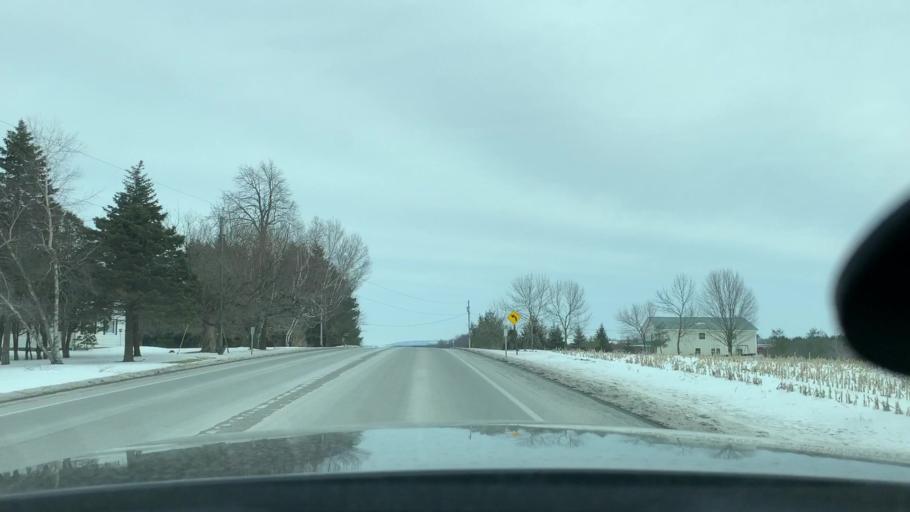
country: US
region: New York
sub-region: Oneida County
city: Utica
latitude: 43.0311
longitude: -75.1737
